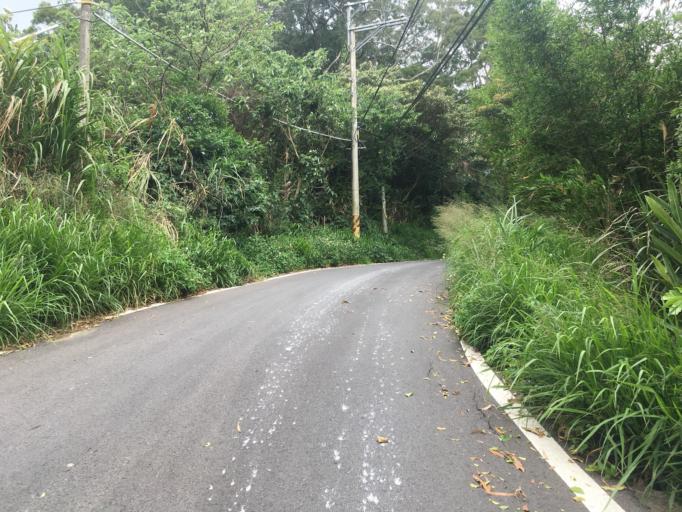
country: TW
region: Taiwan
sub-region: Hsinchu
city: Hsinchu
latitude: 24.7464
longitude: 120.9842
